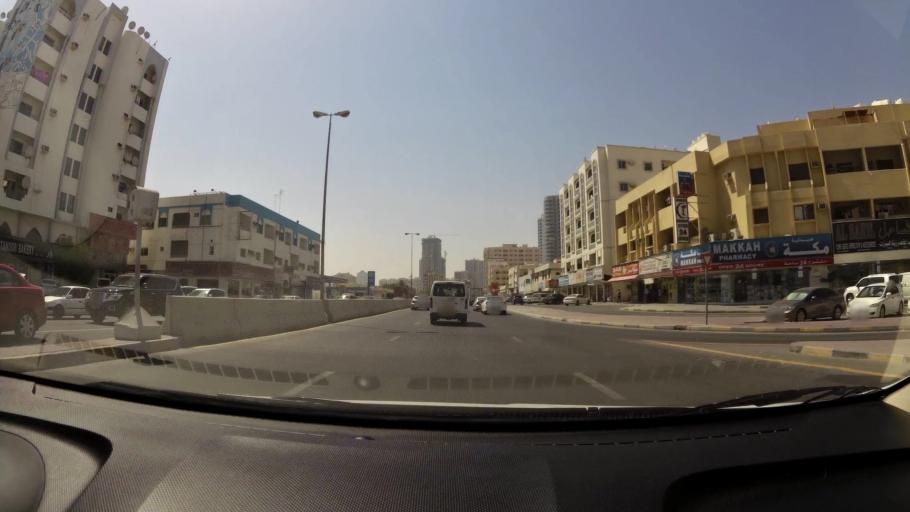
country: AE
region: Ajman
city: Ajman
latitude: 25.4031
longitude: 55.4468
